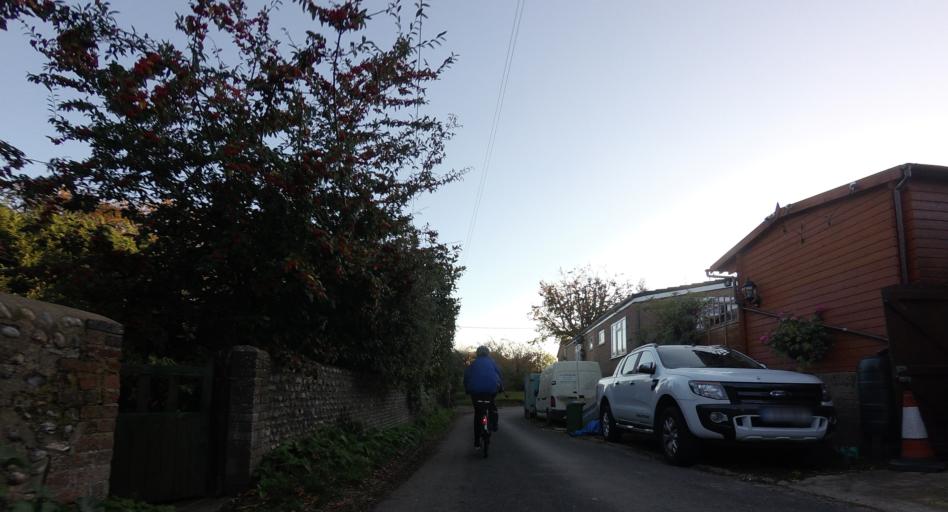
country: GB
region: England
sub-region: West Sussex
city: Steyning
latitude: 50.8906
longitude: -0.3132
